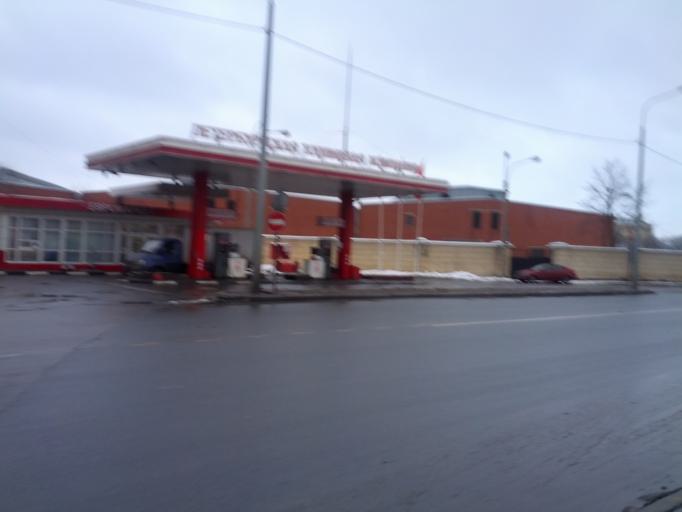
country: RU
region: St.-Petersburg
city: Centralniy
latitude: 59.9076
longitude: 30.3556
